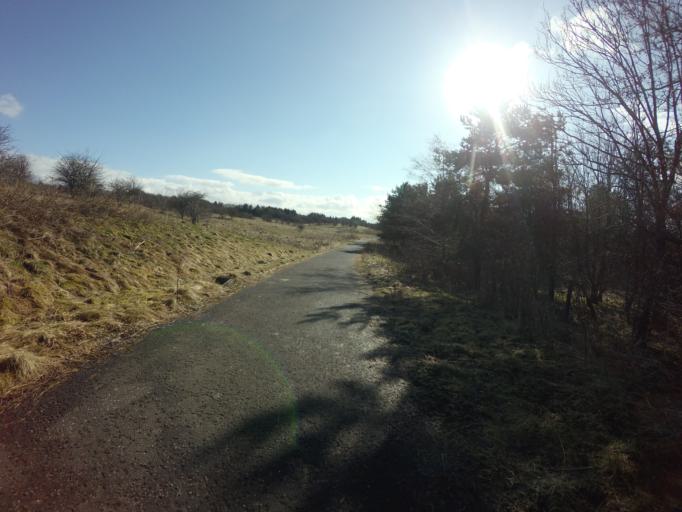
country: GB
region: Scotland
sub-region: West Lothian
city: West Calder
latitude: 55.8925
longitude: -3.5650
